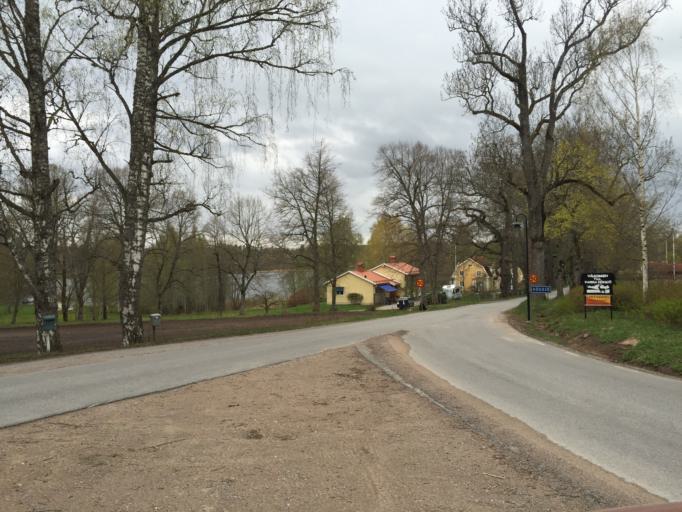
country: SE
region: Soedermanland
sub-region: Vingakers Kommun
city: Vingaker
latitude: 59.0197
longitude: 15.6775
